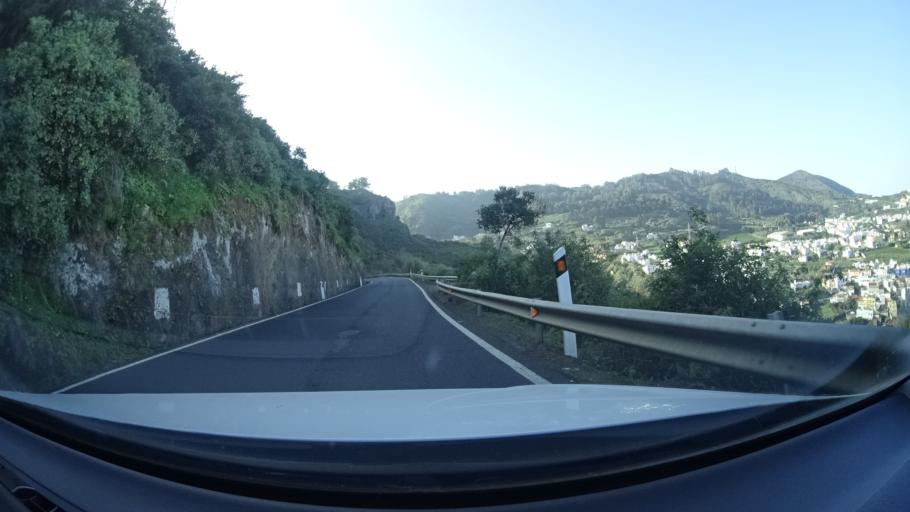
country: ES
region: Canary Islands
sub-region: Provincia de Las Palmas
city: Teror
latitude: 28.0542
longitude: -15.5523
